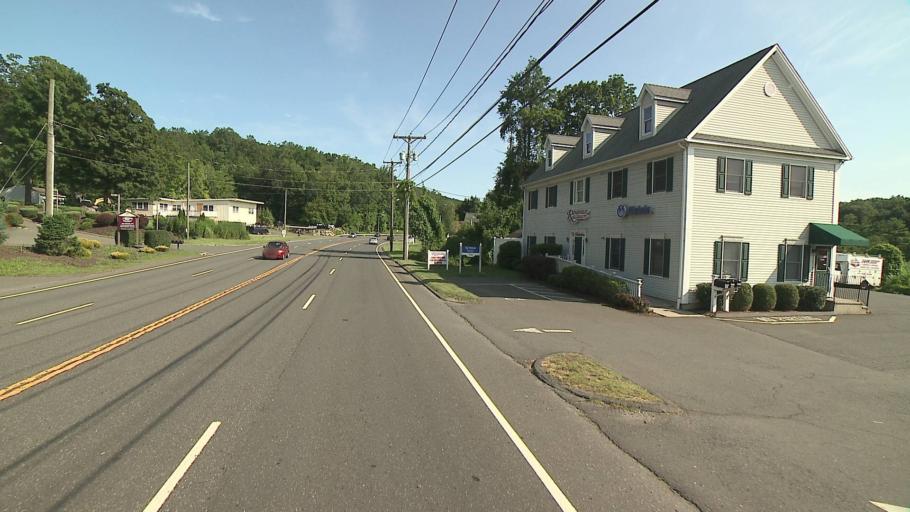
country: US
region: Connecticut
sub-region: Fairfield County
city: Ridgefield
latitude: 41.3283
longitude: -73.4730
